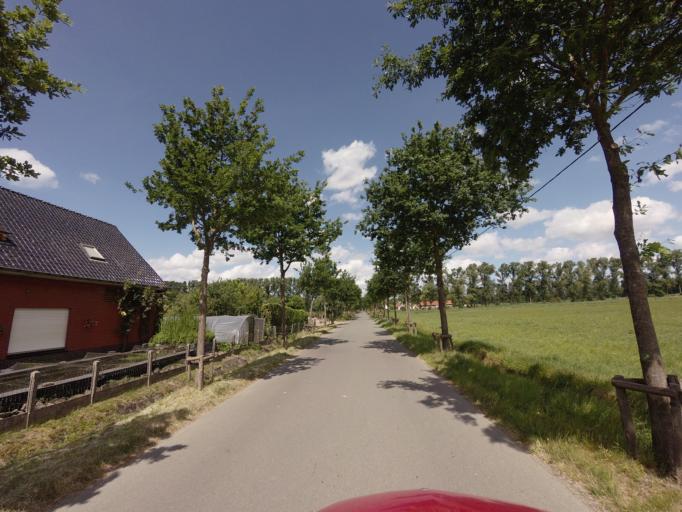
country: BE
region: Flanders
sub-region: Provincie Oost-Vlaanderen
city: Knesselare
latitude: 51.1681
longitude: 3.4142
